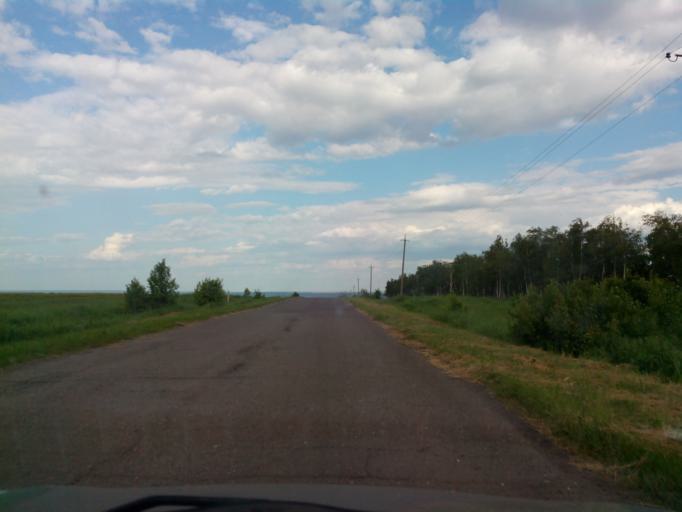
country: RU
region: Volgograd
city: Slashchevskaya
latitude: 49.7958
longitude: 42.4124
